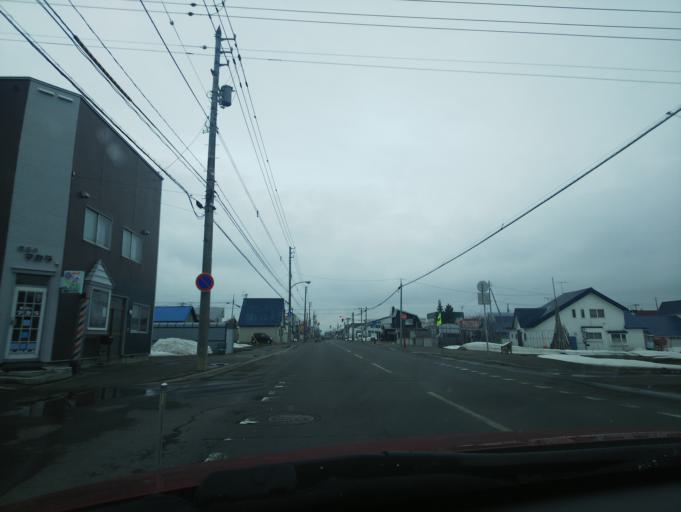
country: JP
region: Hokkaido
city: Nayoro
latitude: 44.3552
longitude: 142.4503
